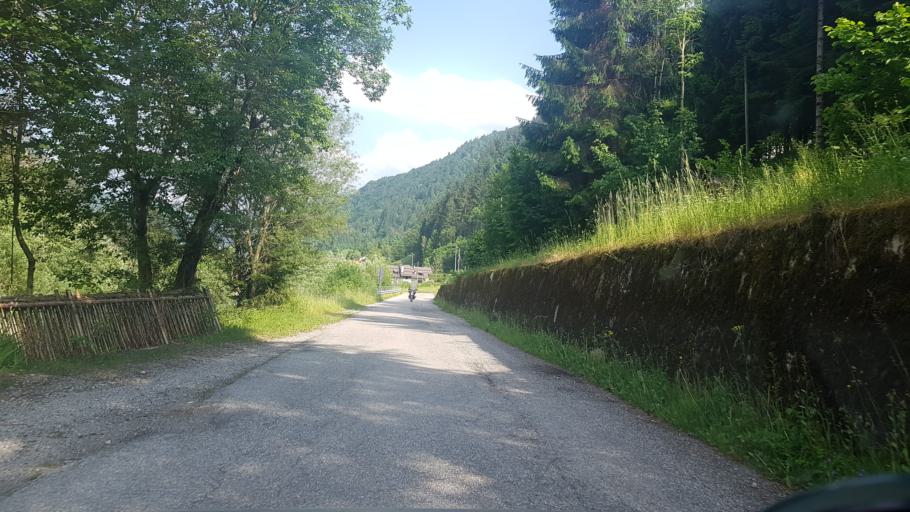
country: IT
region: Friuli Venezia Giulia
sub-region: Provincia di Udine
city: Pontebba
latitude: 46.5235
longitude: 13.2625
